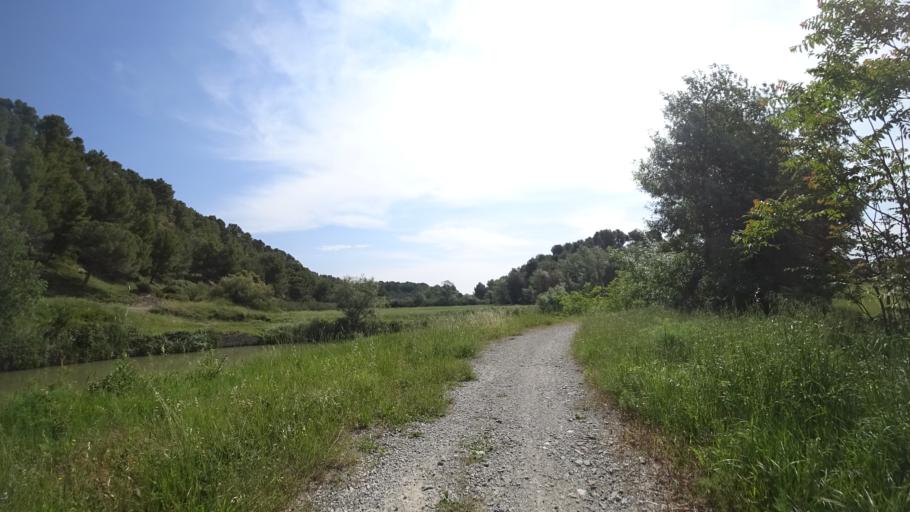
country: FR
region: Languedoc-Roussillon
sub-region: Departement de l'Herault
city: Olonzac
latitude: 43.2487
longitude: 2.7587
